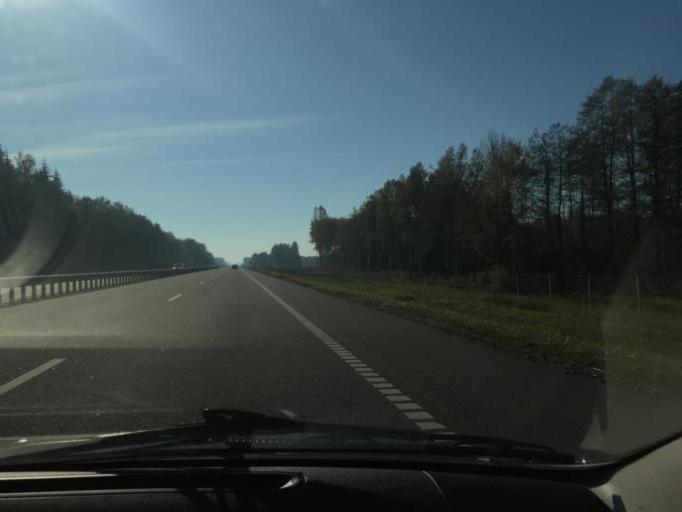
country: BY
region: Minsk
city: Slutsk
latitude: 53.2611
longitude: 27.5501
